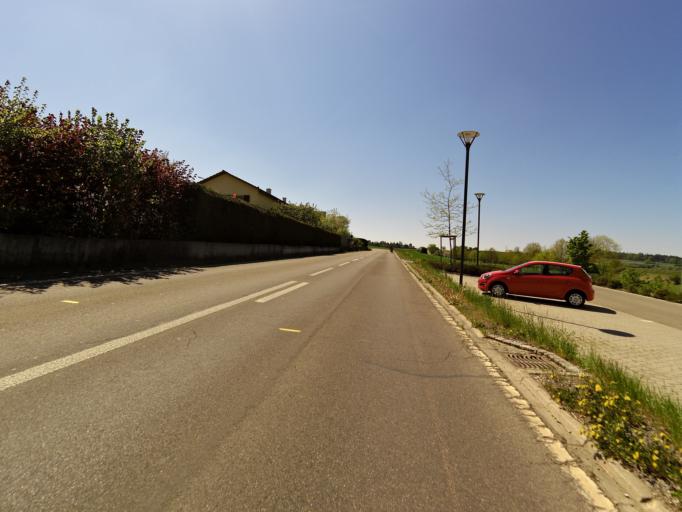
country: CH
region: Thurgau
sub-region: Frauenfeld District
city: Gachnang
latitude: 47.5440
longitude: 8.8393
